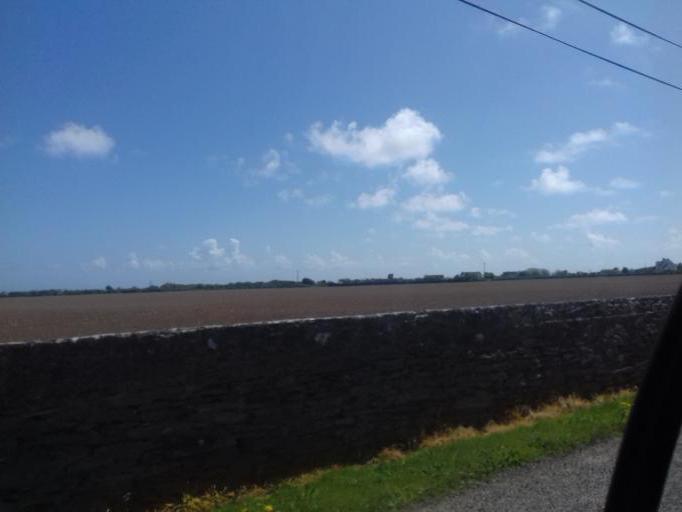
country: IE
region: Munster
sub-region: Waterford
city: Dunmore East
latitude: 52.1403
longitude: -6.9135
